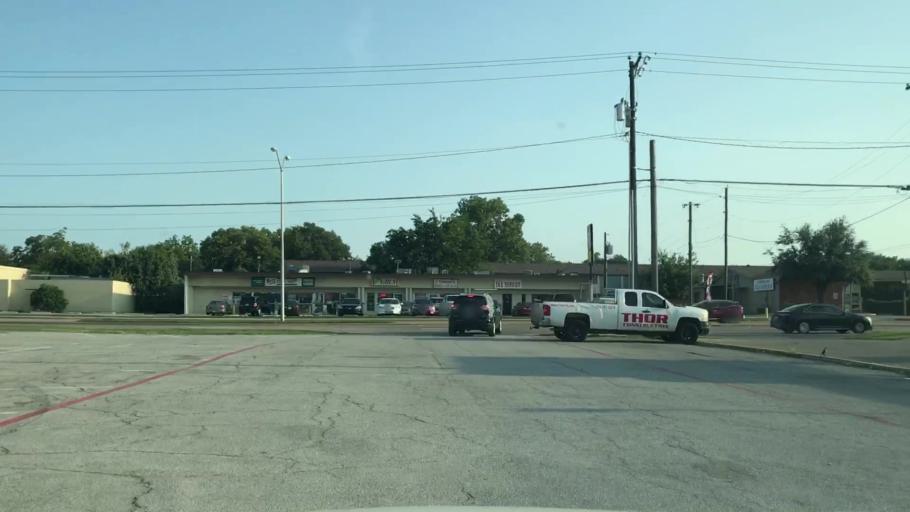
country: US
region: Texas
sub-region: Dallas County
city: Richardson
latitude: 32.8951
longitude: -96.7169
